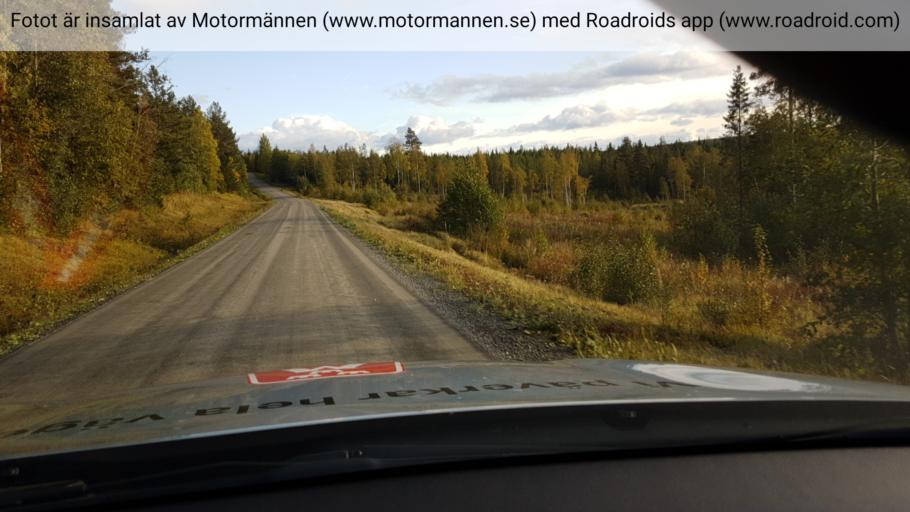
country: SE
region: Jaemtland
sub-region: Krokoms Kommun
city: Krokom
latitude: 63.6926
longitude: 14.5650
